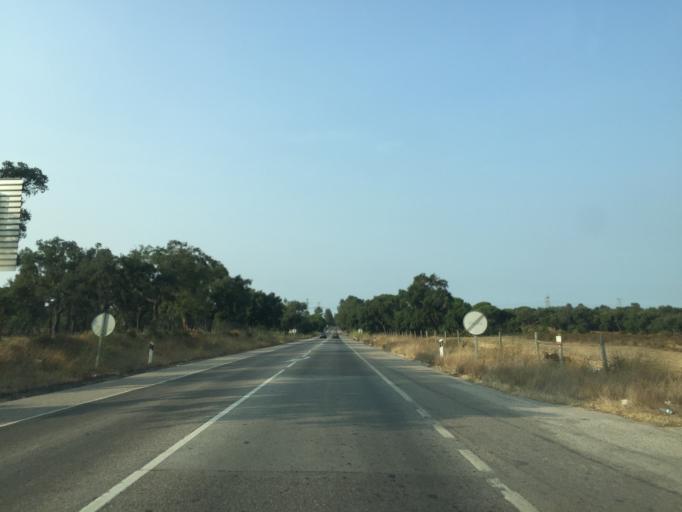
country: PT
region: Setubal
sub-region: Setubal
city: Setubal
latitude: 38.5851
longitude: -8.6790
